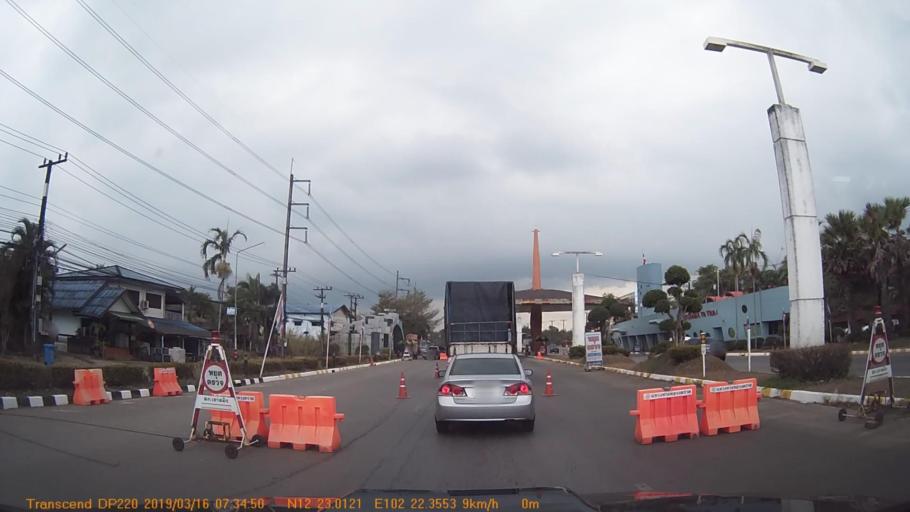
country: TH
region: Trat
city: Khao Saming
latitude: 12.3818
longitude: 102.3735
